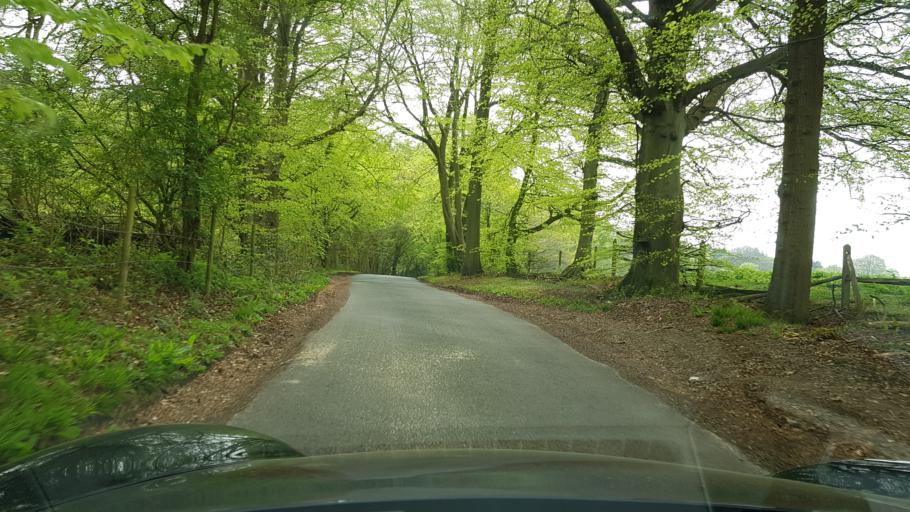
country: GB
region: England
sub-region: Surrey
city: East Horsley
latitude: 51.2393
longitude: -0.4513
